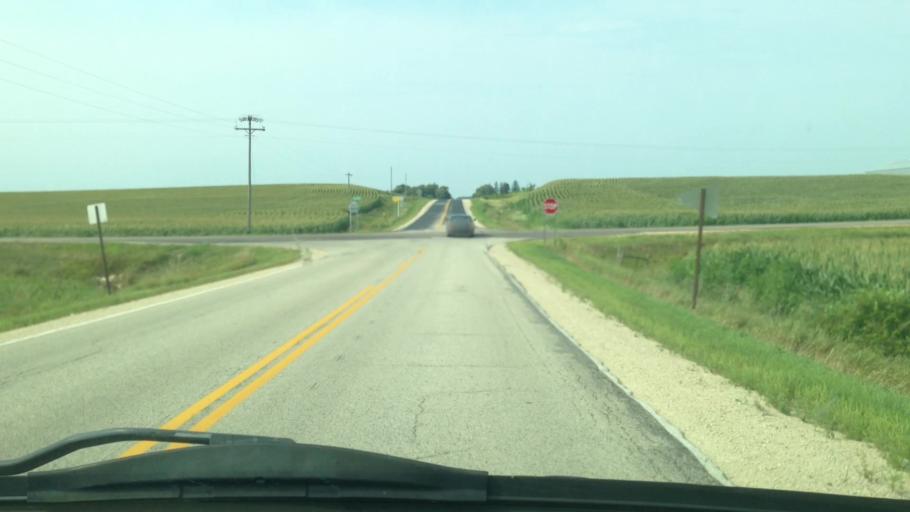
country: US
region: Minnesota
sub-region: Winona County
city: Lewiston
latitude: 43.9003
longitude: -91.9594
